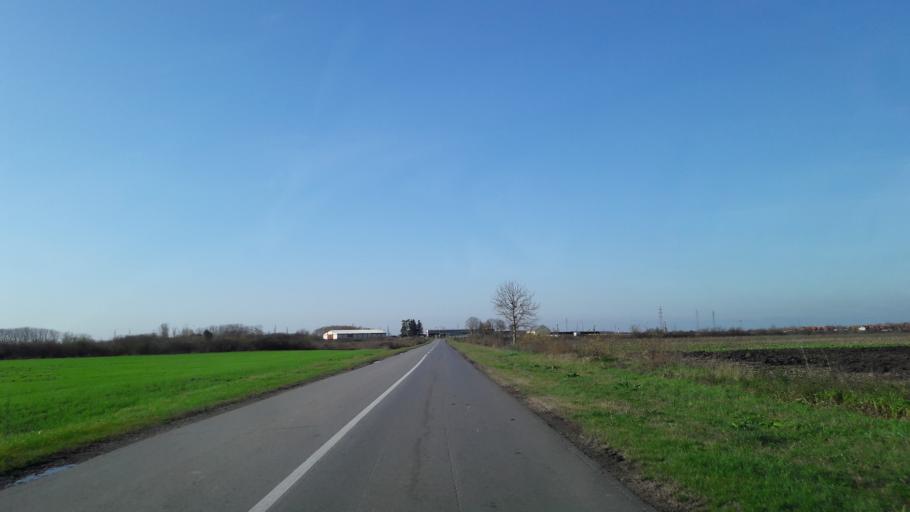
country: HR
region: Osjecko-Baranjska
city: Antunovac
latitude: 45.4757
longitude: 18.6861
